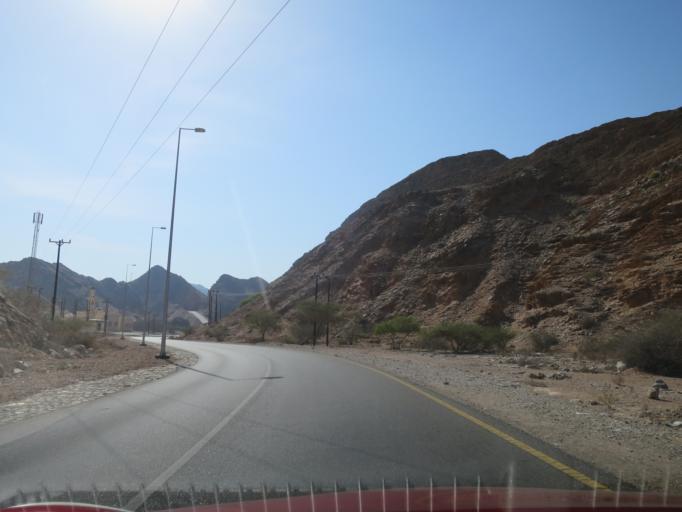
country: OM
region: Muhafazat Masqat
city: Muscat
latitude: 23.5179
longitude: 58.7082
